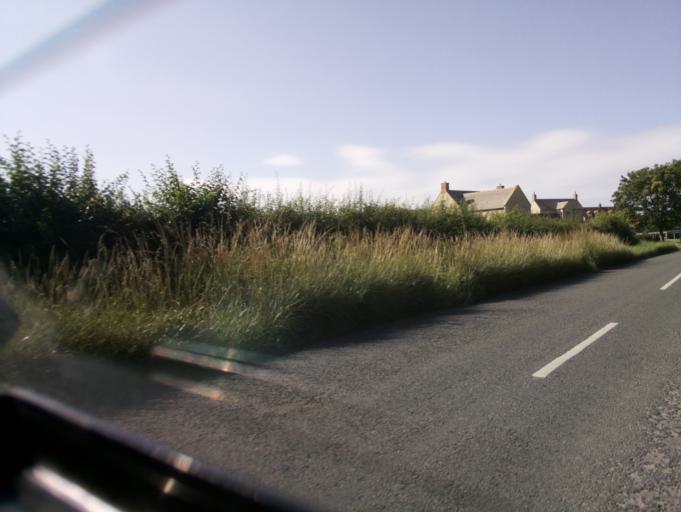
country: GB
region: England
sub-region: Oxfordshire
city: Bampton
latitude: 51.7294
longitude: -1.5069
